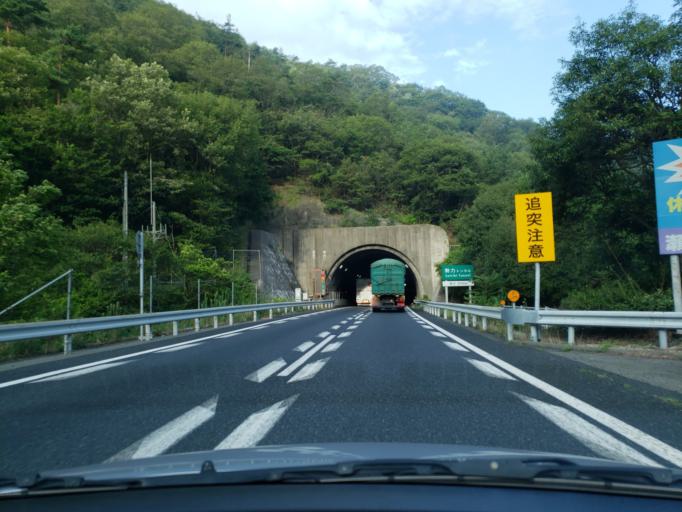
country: JP
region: Okayama
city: Okayama-shi
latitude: 34.7726
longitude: 134.1079
